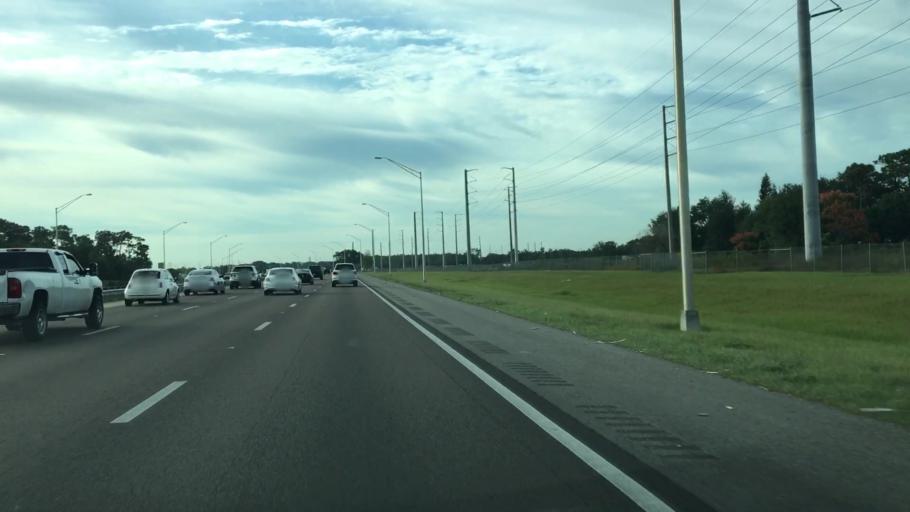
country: US
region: Florida
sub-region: Orange County
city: Azalea Park
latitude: 28.5209
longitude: -81.2509
